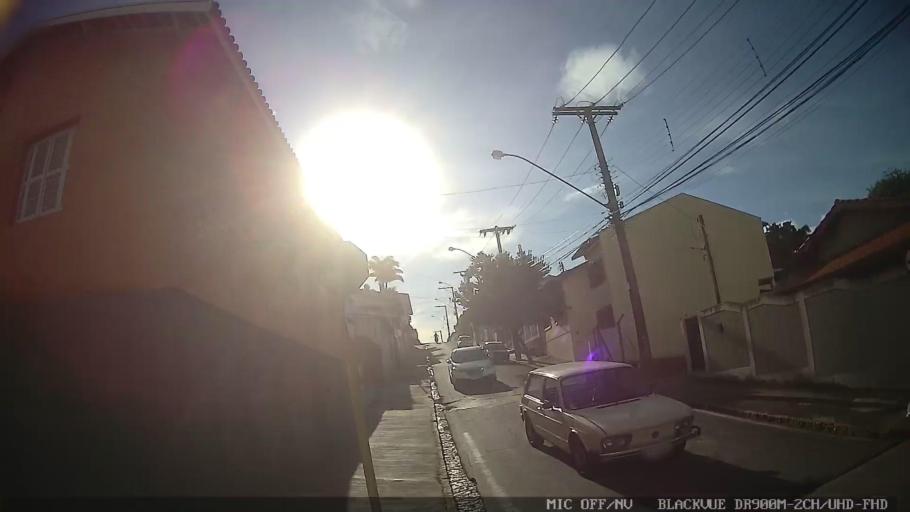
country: BR
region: Sao Paulo
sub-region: Tiete
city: Tiete
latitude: -23.0978
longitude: -47.7145
